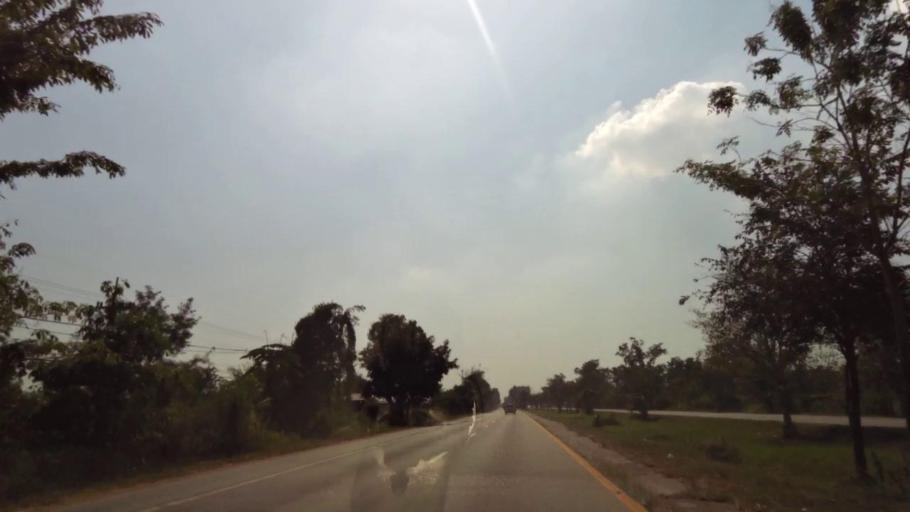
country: TH
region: Phichit
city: Wachira Barami
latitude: 16.5376
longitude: 100.1444
